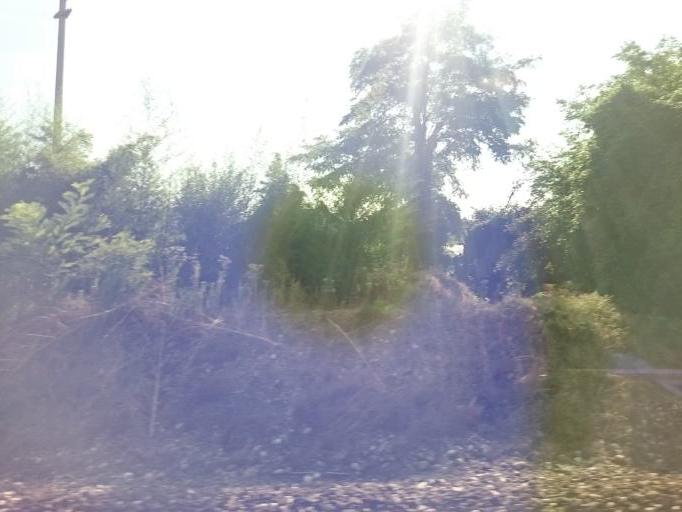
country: IT
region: Veneto
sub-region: Provincia di Verona
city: Parona
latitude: 45.4606
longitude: 10.9388
